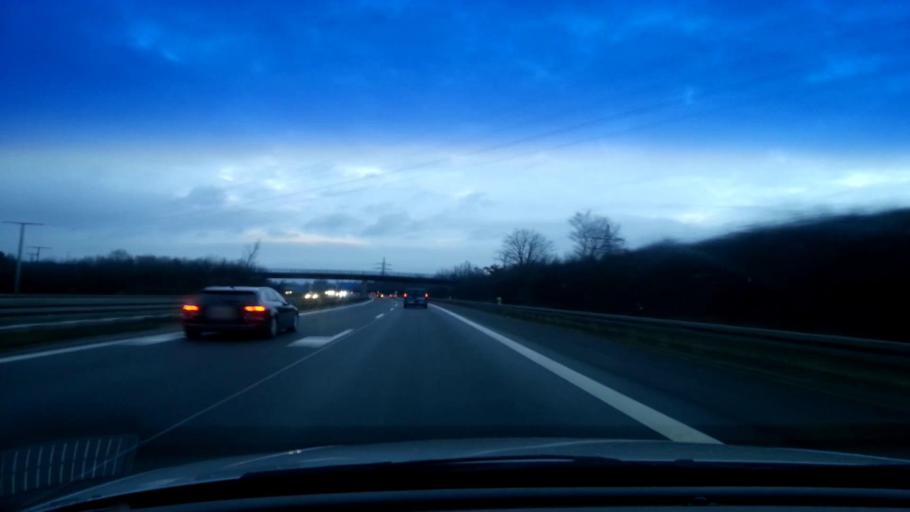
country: DE
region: Bavaria
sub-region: Upper Franconia
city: Gundelsheim
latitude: 49.9245
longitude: 10.9039
